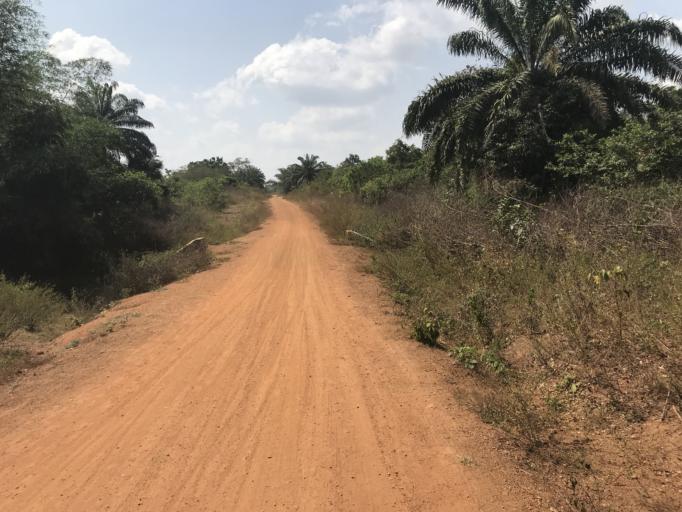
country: NG
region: Osun
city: Ifon
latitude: 7.9781
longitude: 4.5335
